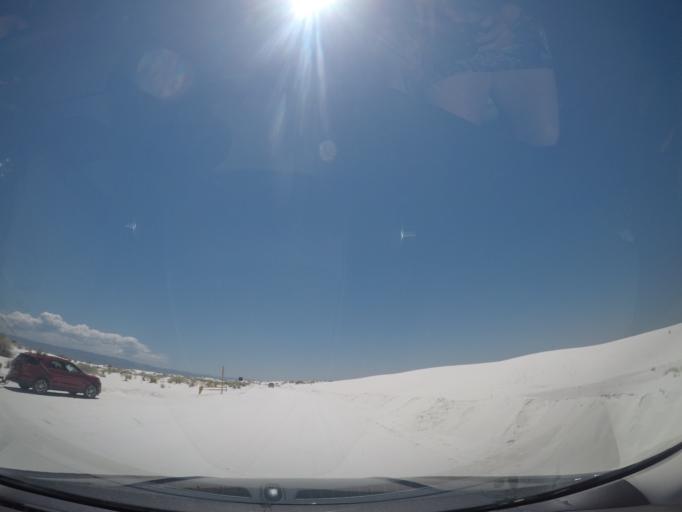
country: US
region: New Mexico
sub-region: Otero County
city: Holloman Air Force Base
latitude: 32.7976
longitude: -106.2490
